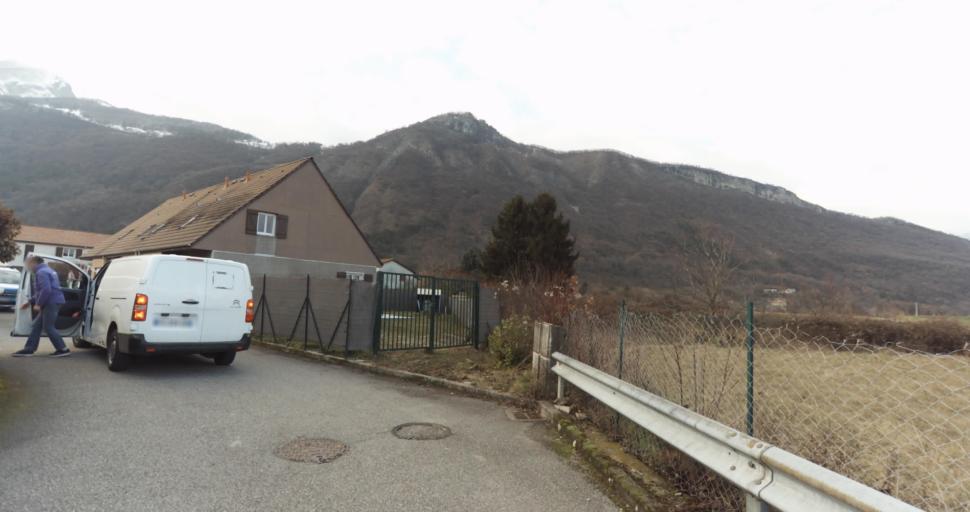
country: FR
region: Rhone-Alpes
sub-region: Departement de l'Isere
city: Vif
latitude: 45.0619
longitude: 5.6743
